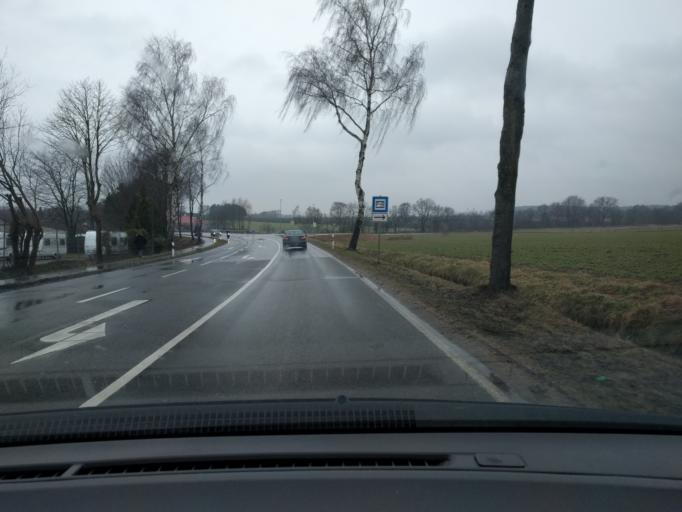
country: DE
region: Lower Saxony
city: Bendestorf
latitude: 53.3662
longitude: 9.9325
